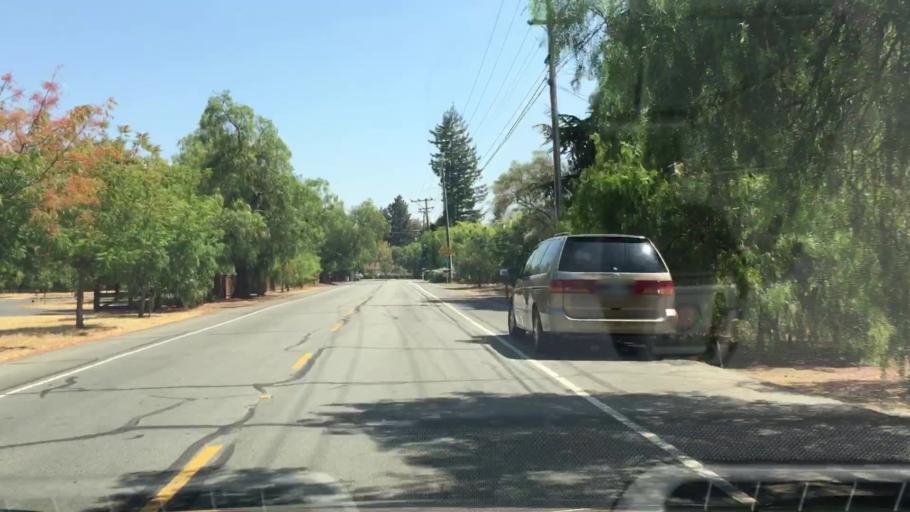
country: US
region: California
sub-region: Santa Clara County
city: Loyola
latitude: 37.3674
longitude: -122.1036
